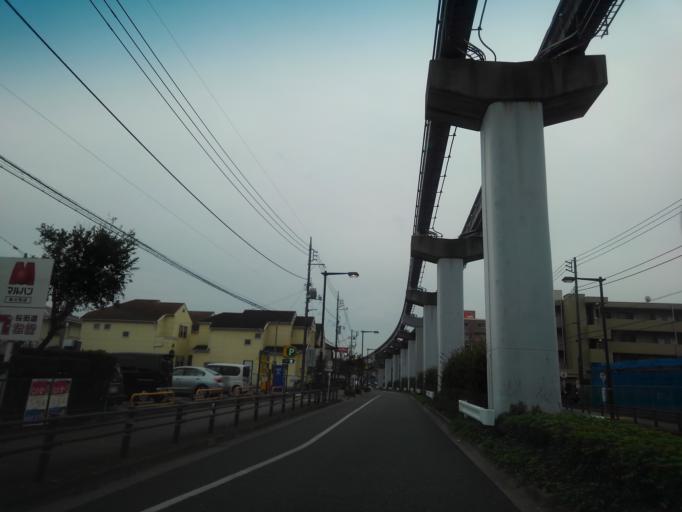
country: JP
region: Tokyo
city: Higashimurayama-shi
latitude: 35.7445
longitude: 139.4159
